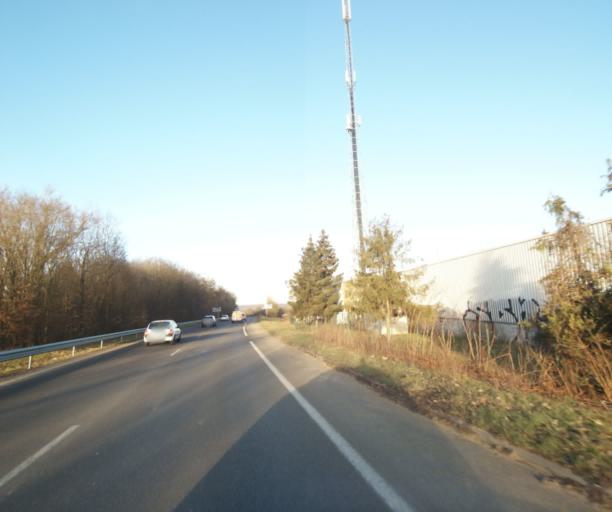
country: FR
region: Lorraine
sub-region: Departement de Meurthe-et-Moselle
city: Laxou
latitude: 48.6951
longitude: 6.1217
